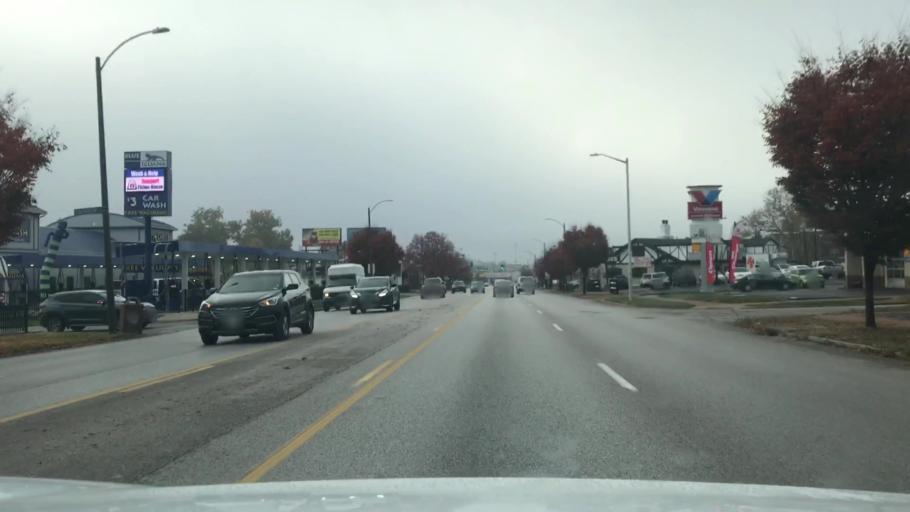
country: US
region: Missouri
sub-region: Saint Louis County
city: Maplewood
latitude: 38.5979
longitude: -90.2707
